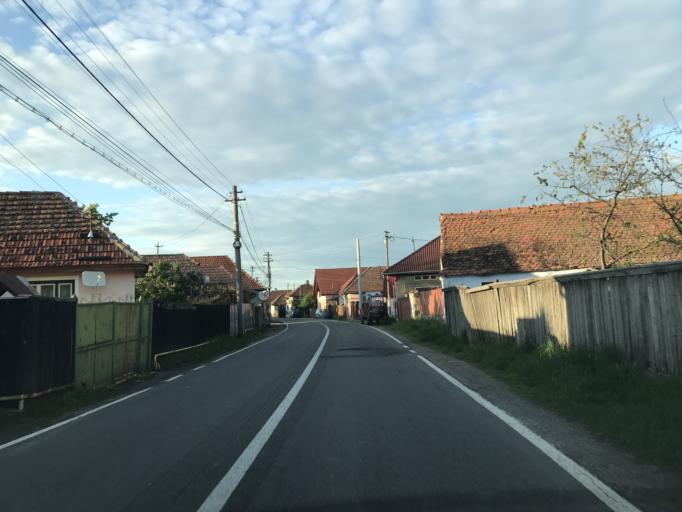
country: RO
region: Sibiu
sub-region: Comuna Cartisoara
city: Cartisoara
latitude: 45.7219
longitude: 24.5721
